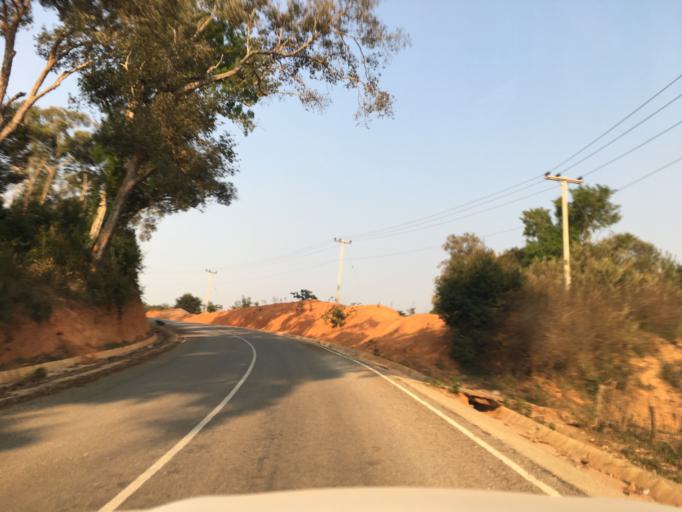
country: LA
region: Houaphan
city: Xam Nua
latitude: 20.6037
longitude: 104.0724
